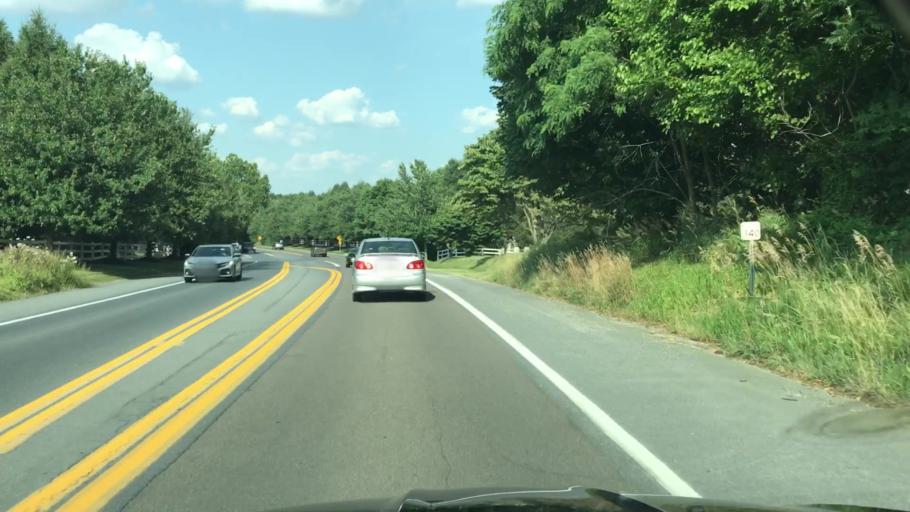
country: US
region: Pennsylvania
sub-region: York County
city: Dillsburg
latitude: 40.1611
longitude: -77.0167
